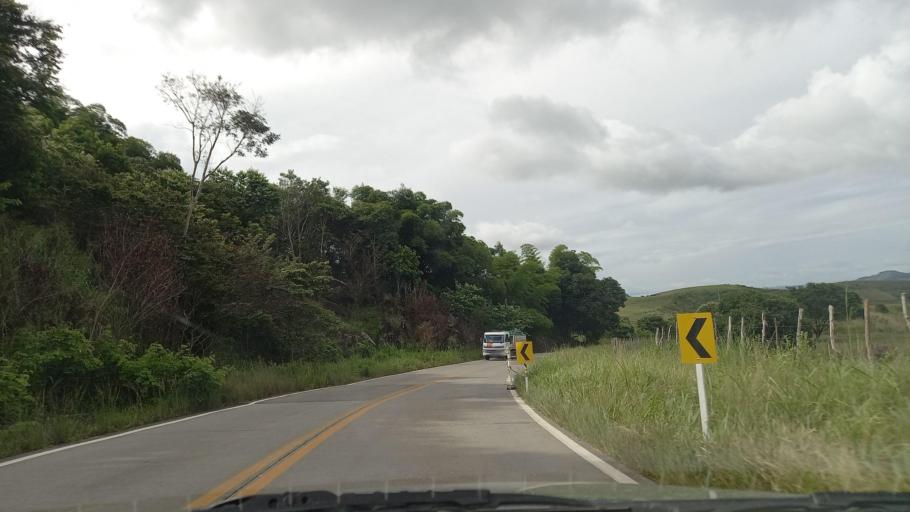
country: BR
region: Pernambuco
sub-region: Maraial
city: Maraial
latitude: -8.7788
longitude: -35.8709
